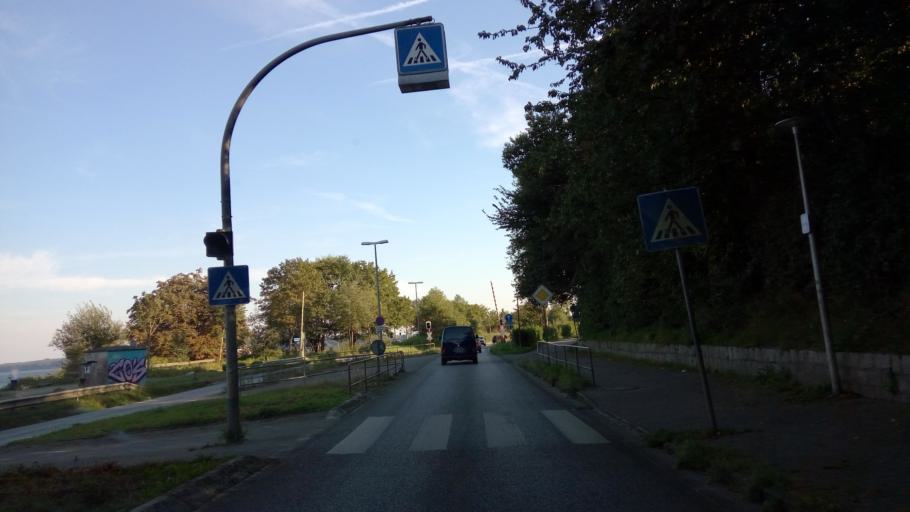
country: DE
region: Schleswig-Holstein
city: Eckernforde
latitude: 54.4593
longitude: 9.8436
